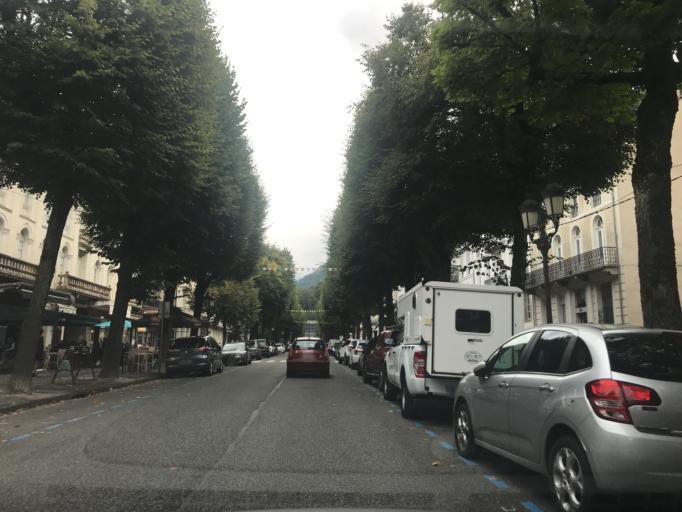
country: FR
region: Midi-Pyrenees
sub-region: Departement de la Haute-Garonne
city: Bagneres-de-Luchon
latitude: 42.7877
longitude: 0.5929
